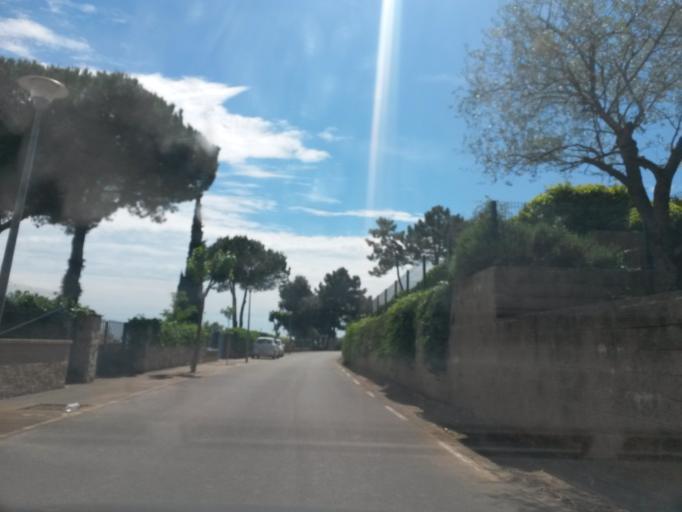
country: ES
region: Catalonia
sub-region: Provincia de Girona
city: Vilablareix
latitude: 41.9623
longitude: 2.7618
